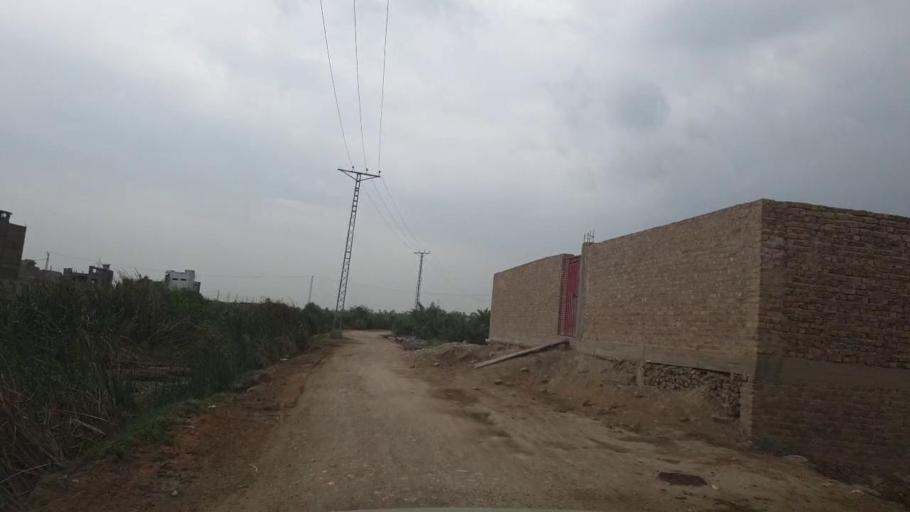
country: PK
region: Sindh
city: Khairpur
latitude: 27.5329
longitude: 68.7328
